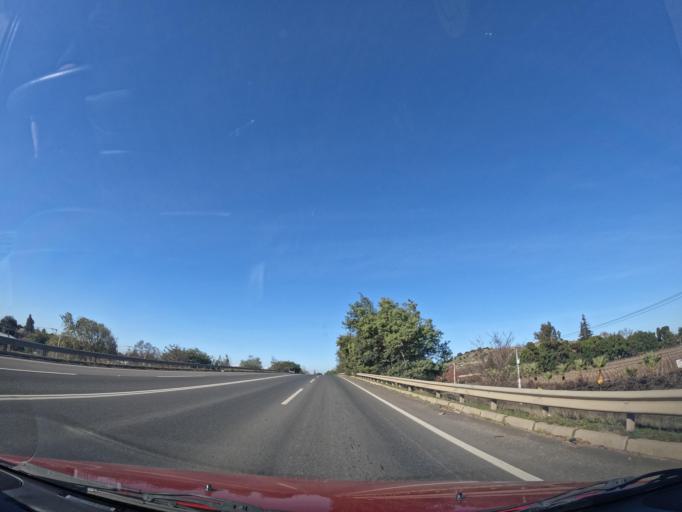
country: CL
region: Maule
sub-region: Provincia de Linares
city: San Javier
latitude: -35.6252
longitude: -71.7501
